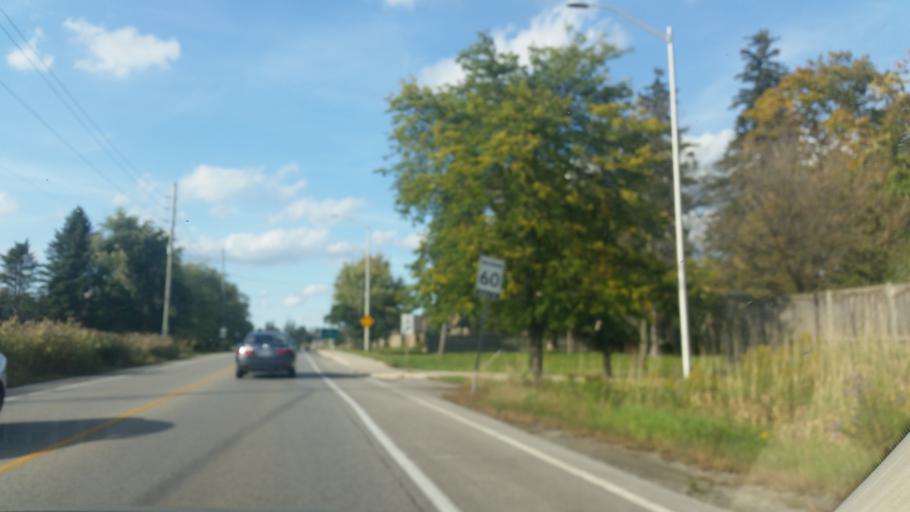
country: CA
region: Ontario
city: London
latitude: 43.0275
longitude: -81.3153
